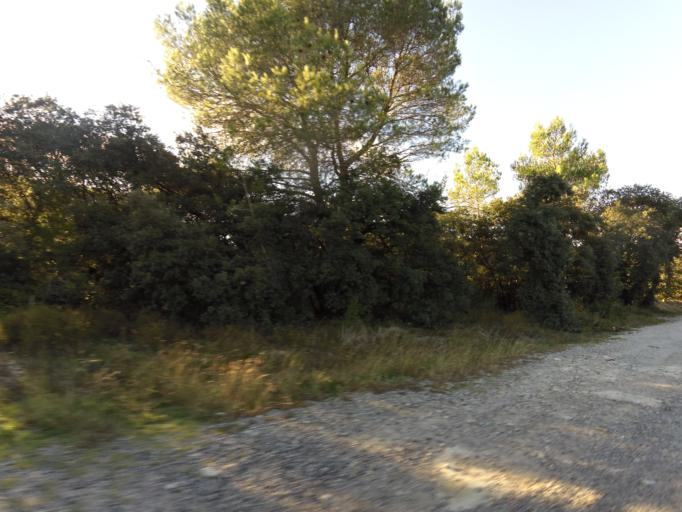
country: FR
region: Languedoc-Roussillon
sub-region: Departement du Gard
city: Villevieille
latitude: 43.7951
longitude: 4.1185
